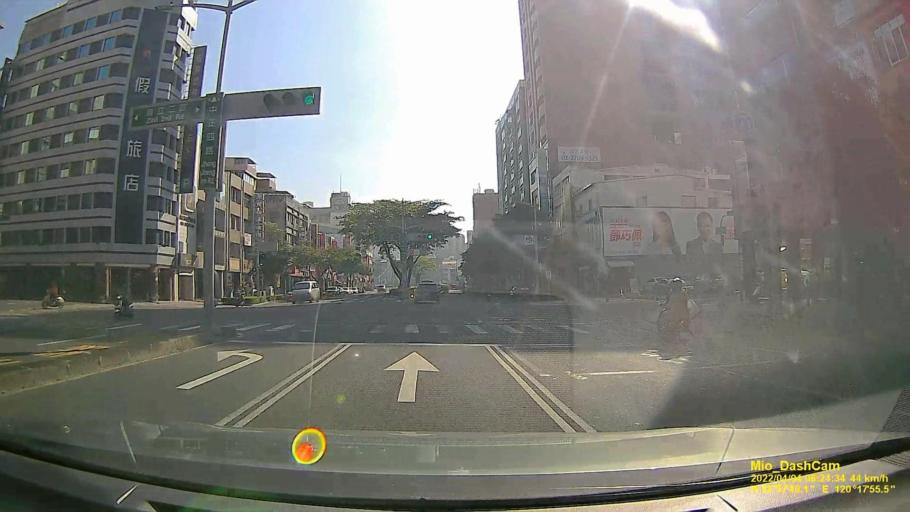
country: TW
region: Kaohsiung
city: Kaohsiung
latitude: 22.6303
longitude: 120.2989
